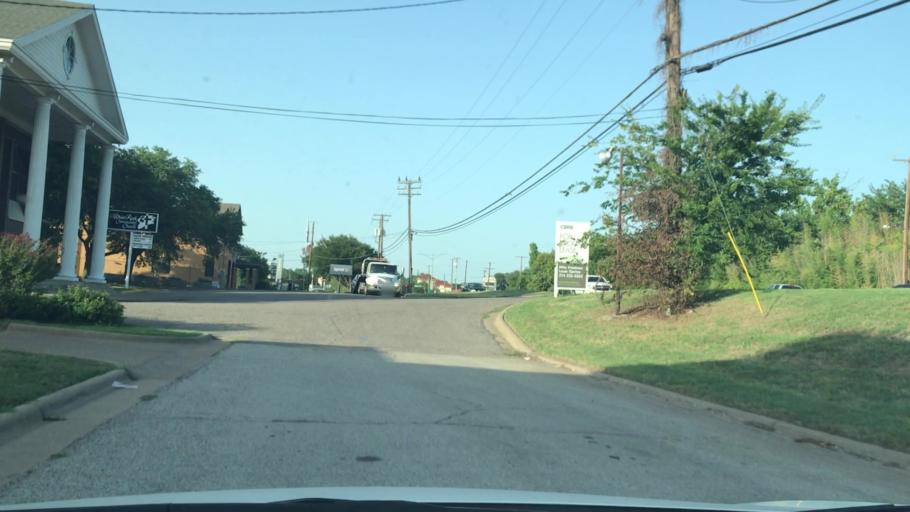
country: US
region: Texas
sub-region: Dallas County
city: Highland Park
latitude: 32.8319
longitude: -96.7049
